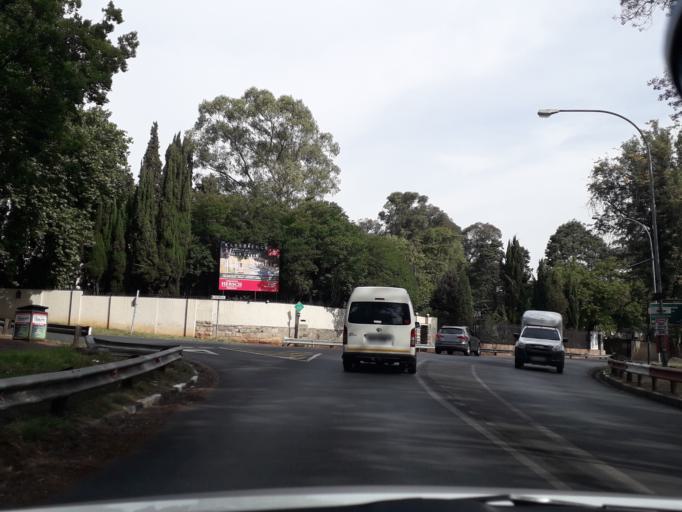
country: ZA
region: Gauteng
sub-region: City of Johannesburg Metropolitan Municipality
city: Johannesburg
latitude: -26.1595
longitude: 28.0351
